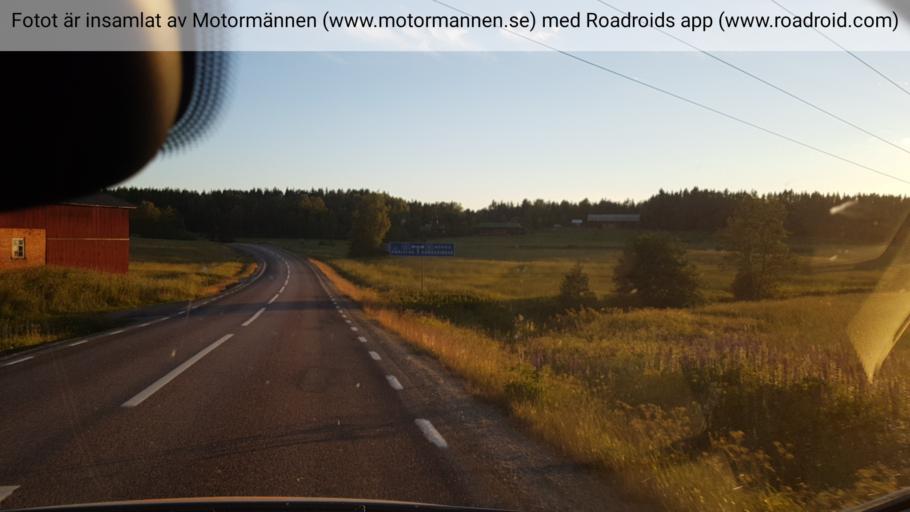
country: SE
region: Vaermland
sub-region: Sunne Kommun
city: Sunne
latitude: 59.6576
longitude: 12.9500
